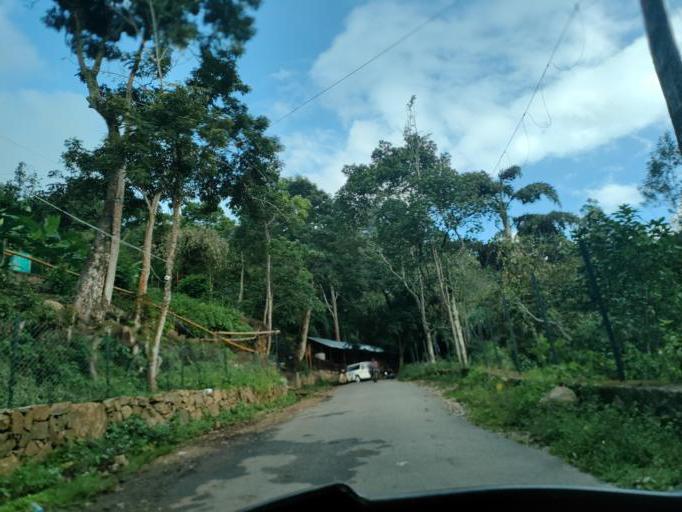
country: IN
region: Tamil Nadu
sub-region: Dindigul
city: Kodaikanal
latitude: 10.2759
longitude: 77.5335
